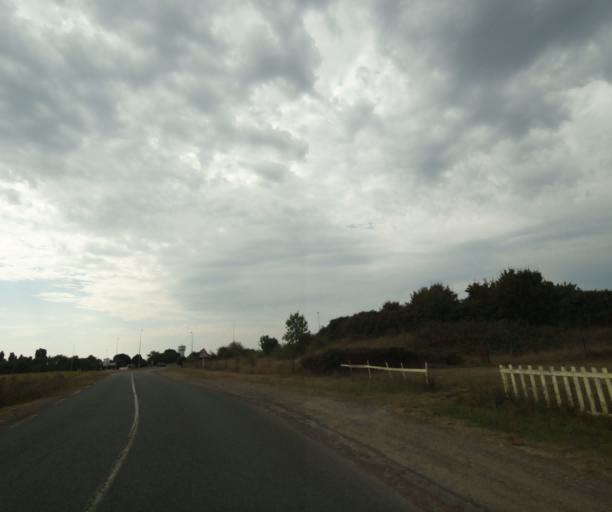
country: FR
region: Poitou-Charentes
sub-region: Departement de la Charente-Maritime
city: Tonnay-Charente
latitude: 45.9553
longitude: -0.8788
